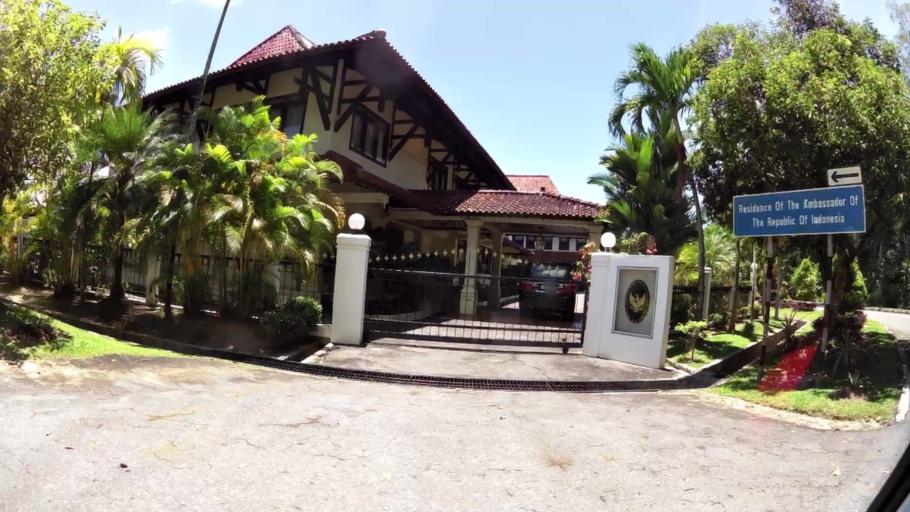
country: BN
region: Brunei and Muara
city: Bandar Seri Begawan
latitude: 4.9224
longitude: 114.9658
